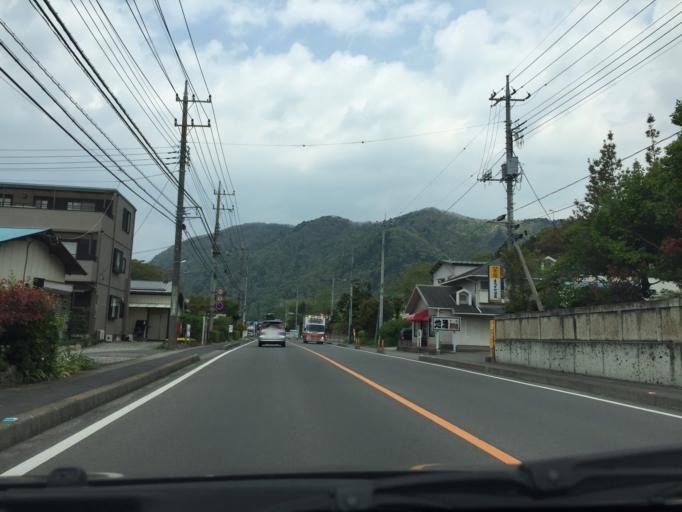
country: JP
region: Tochigi
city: Imaichi
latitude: 36.8156
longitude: 139.7144
